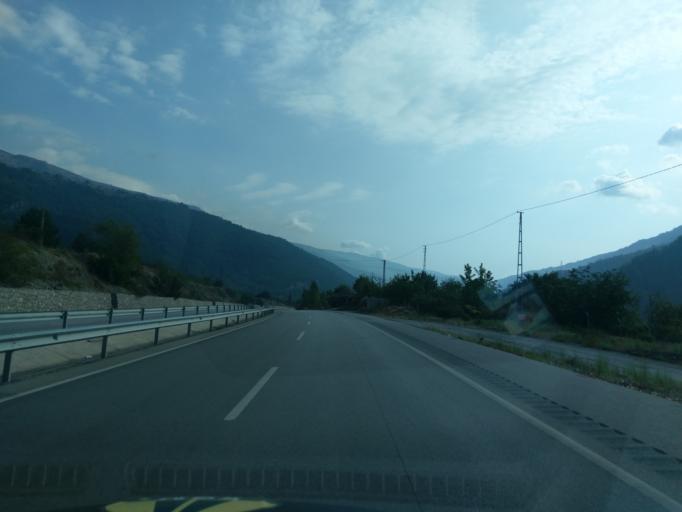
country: TR
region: Amasya
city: Akdag
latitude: 40.7444
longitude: 36.0152
